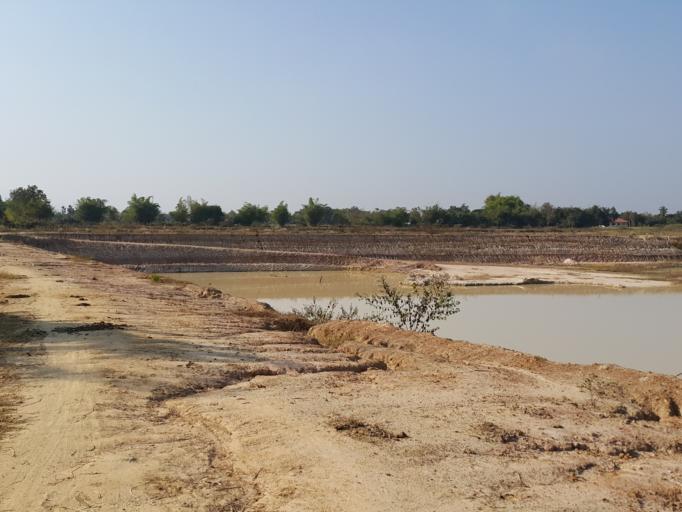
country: TH
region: Chiang Mai
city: San Kamphaeng
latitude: 18.7971
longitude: 99.0920
